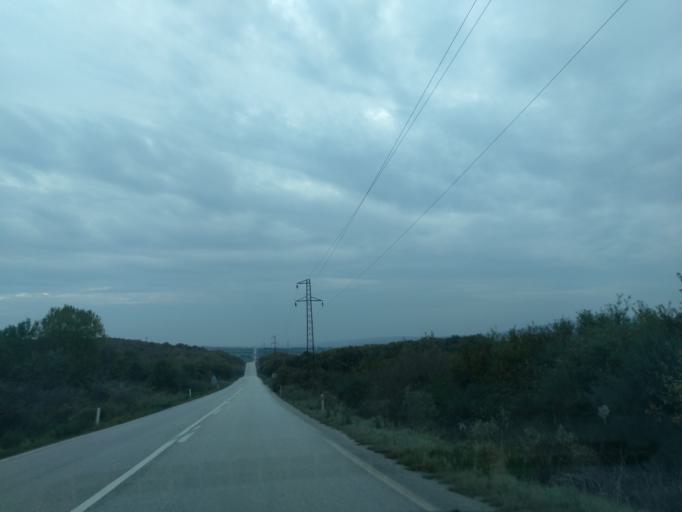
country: TR
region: Istanbul
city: Canta
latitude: 41.1586
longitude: 28.1068
